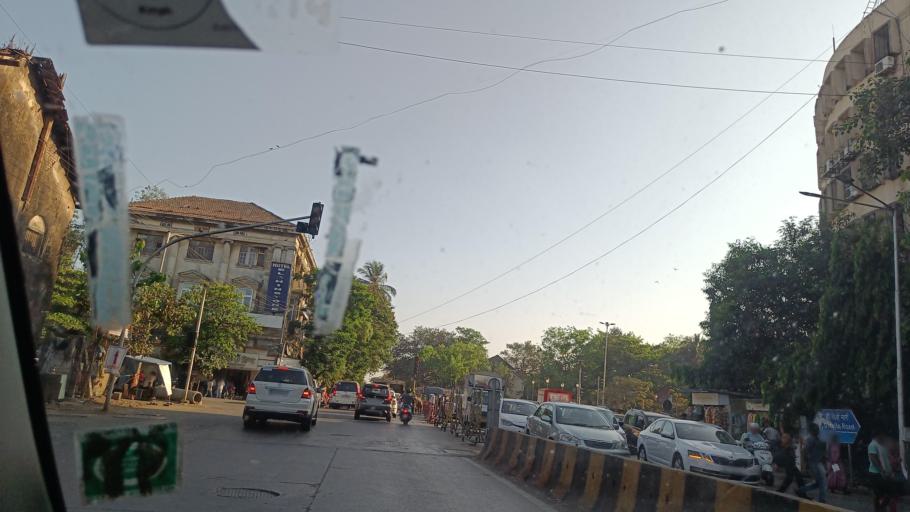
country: IN
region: Maharashtra
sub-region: Raigarh
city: Uran
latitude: 18.9495
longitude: 72.8407
